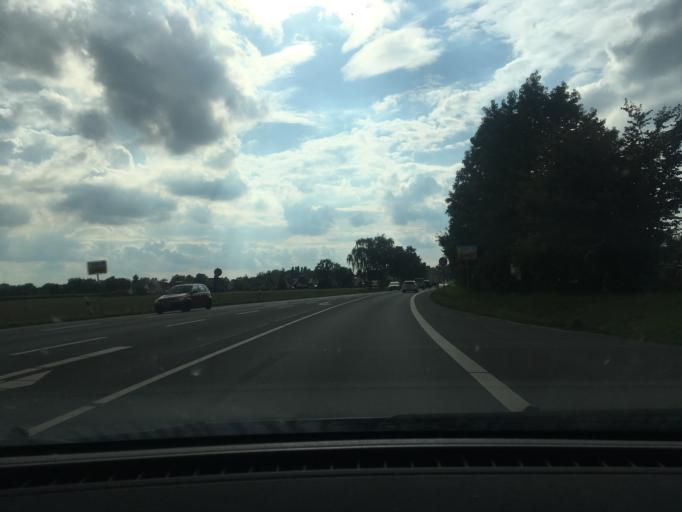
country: DE
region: Lower Saxony
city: Celle
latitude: 52.6366
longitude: 10.1056
